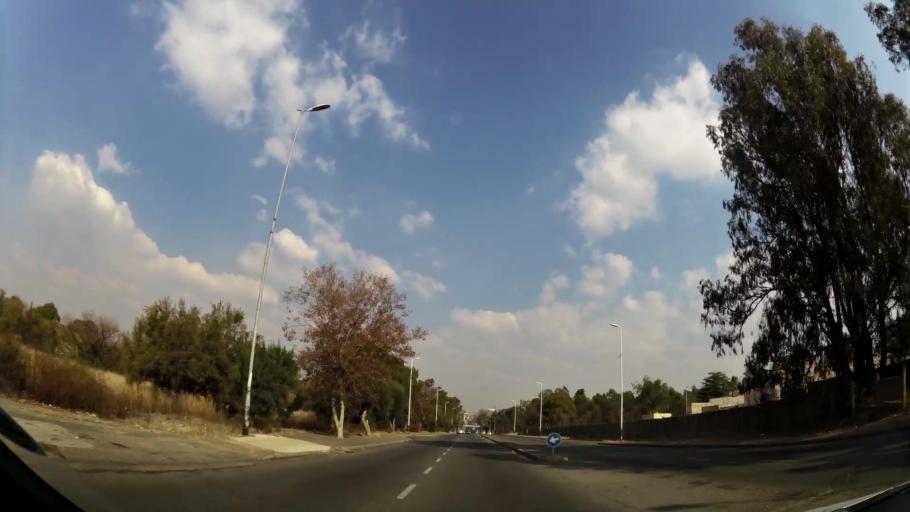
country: ZA
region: Gauteng
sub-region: Ekurhuleni Metropolitan Municipality
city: Boksburg
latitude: -26.2155
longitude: 28.2535
